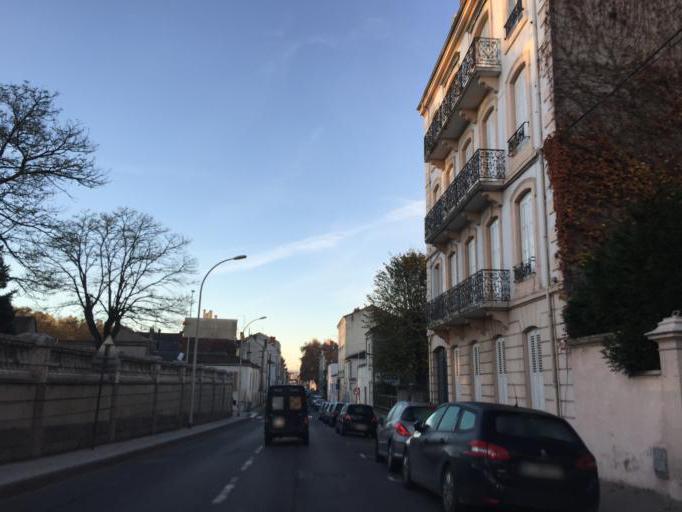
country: FR
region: Rhone-Alpes
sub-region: Departement de la Loire
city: Roanne
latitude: 46.0332
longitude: 4.0773
